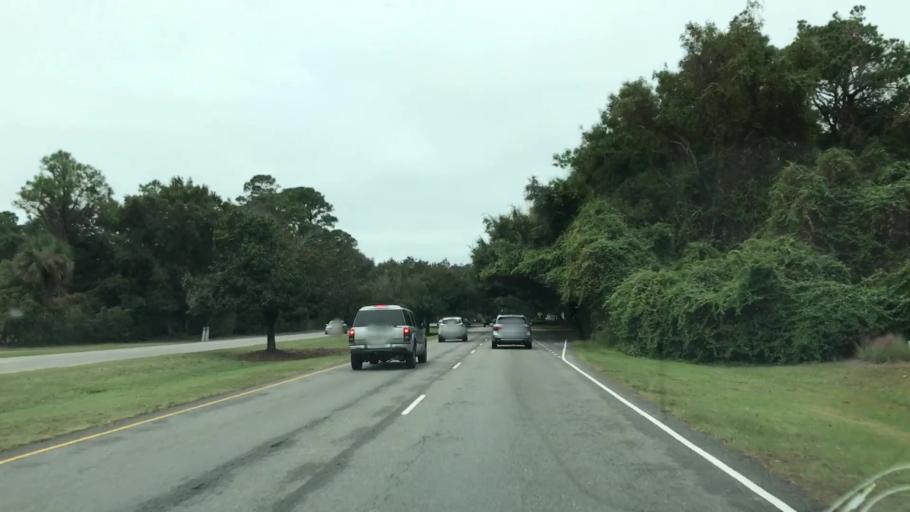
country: US
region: South Carolina
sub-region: Beaufort County
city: Hilton Head Island
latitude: 32.1882
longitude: -80.7140
